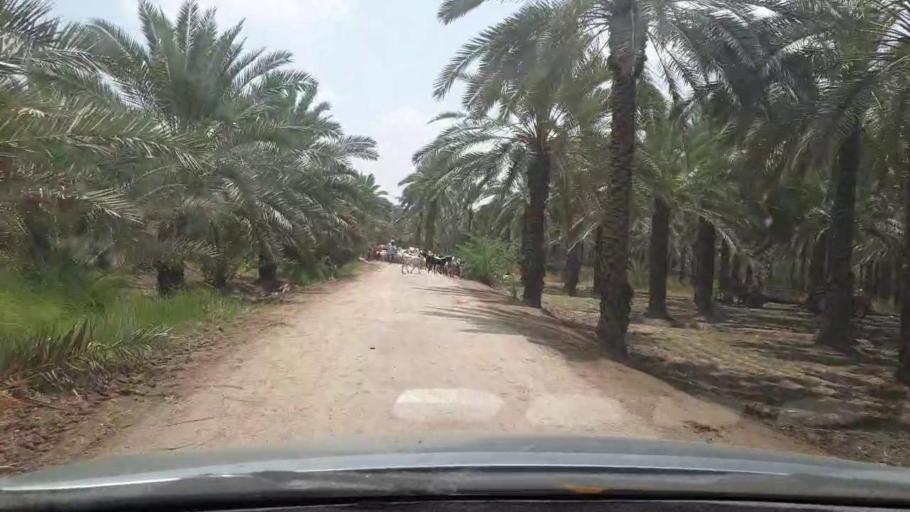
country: PK
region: Sindh
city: Khairpur
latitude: 27.4605
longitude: 68.7188
